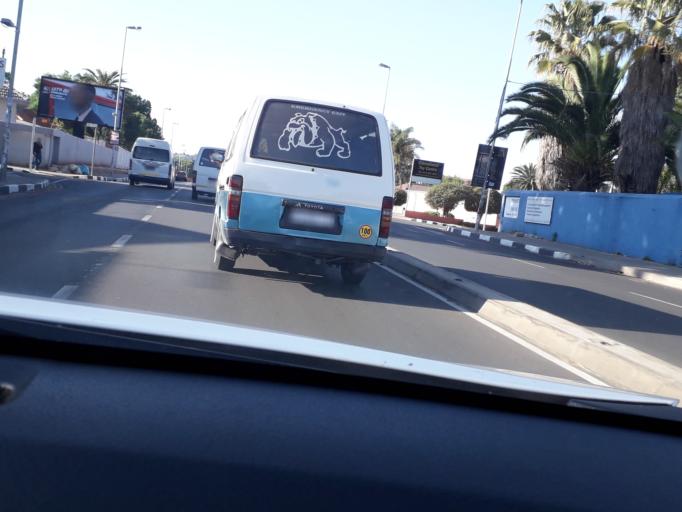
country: ZA
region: Gauteng
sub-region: City of Johannesburg Metropolitan Municipality
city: Johannesburg
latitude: -26.1422
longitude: 28.0867
